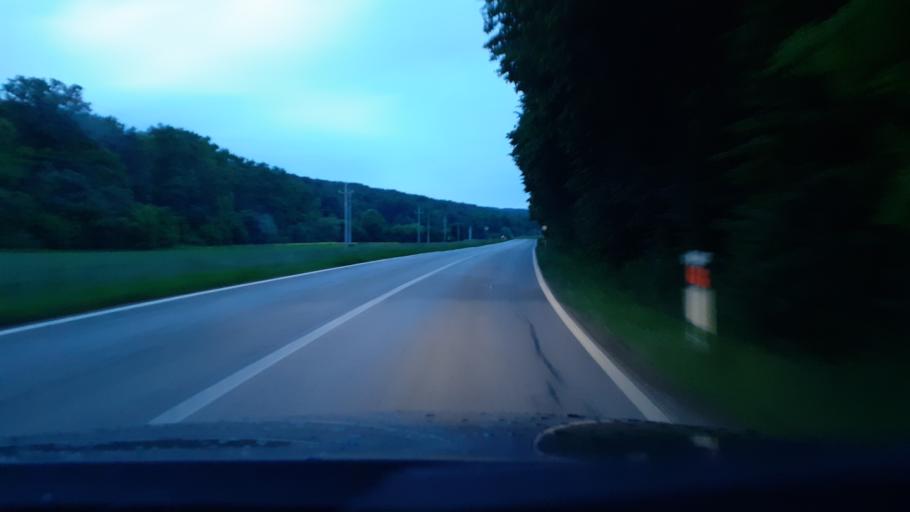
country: HR
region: Pozesko-Slavonska
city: Bilice
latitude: 45.1893
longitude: 17.8556
